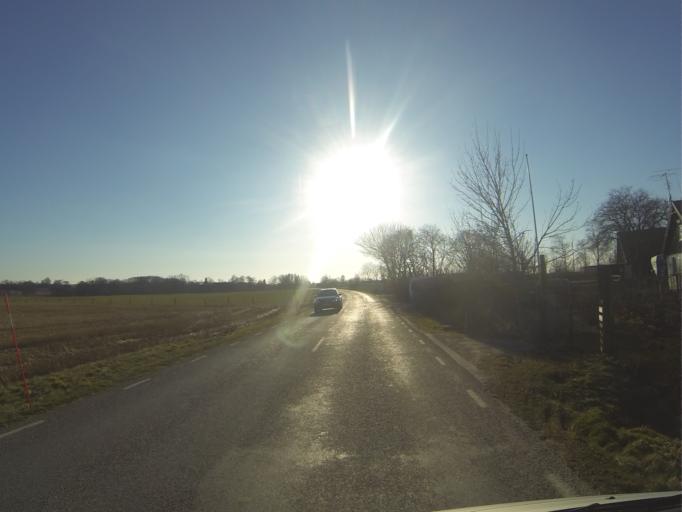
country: SE
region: Skane
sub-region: Hoors Kommun
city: Loberod
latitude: 55.7989
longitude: 13.5699
